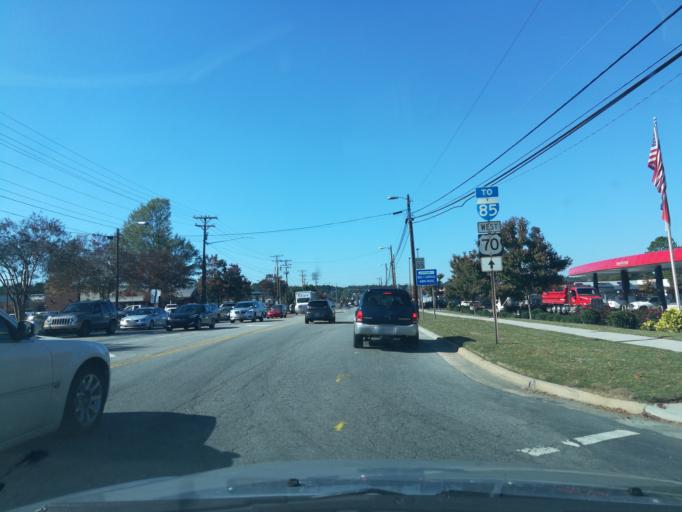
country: US
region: North Carolina
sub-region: Durham County
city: Durham
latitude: 36.0192
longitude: -78.9457
